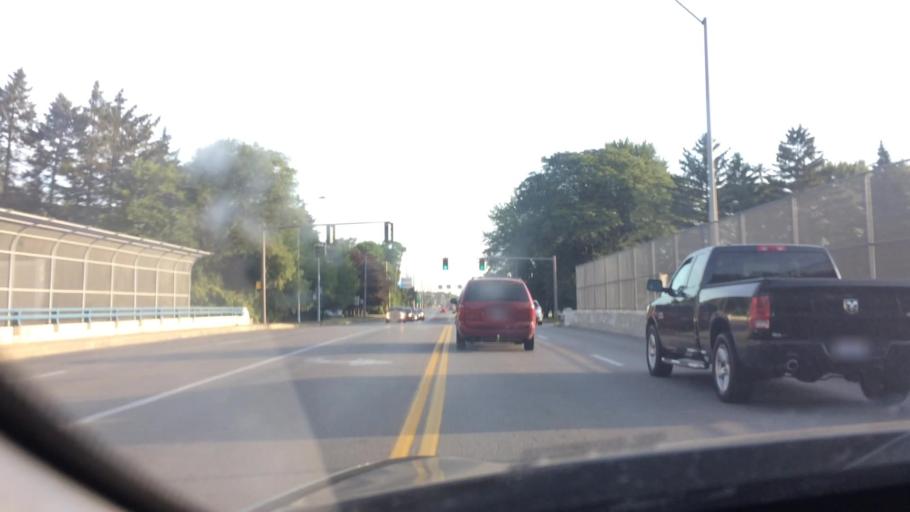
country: US
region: Ohio
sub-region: Lucas County
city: Ottawa Hills
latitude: 41.6878
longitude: -83.6444
